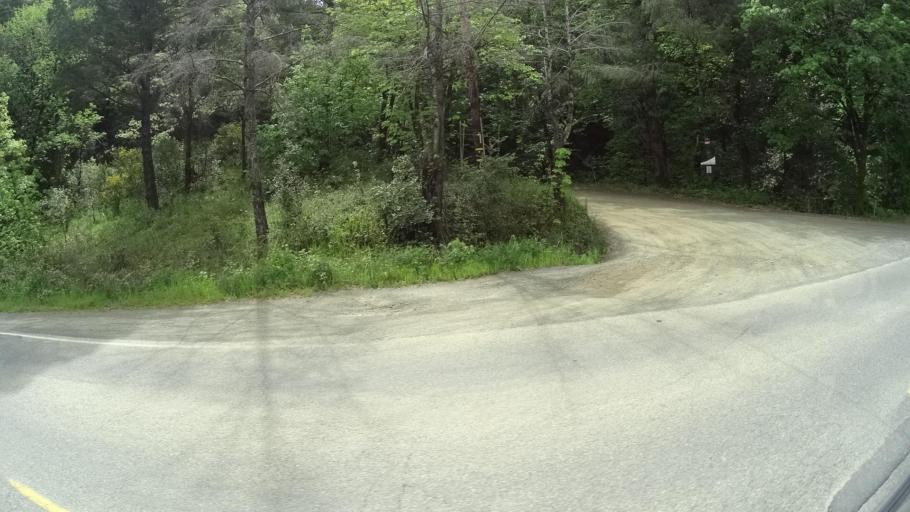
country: US
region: California
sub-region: Humboldt County
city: Redway
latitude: 40.1294
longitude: -123.8624
